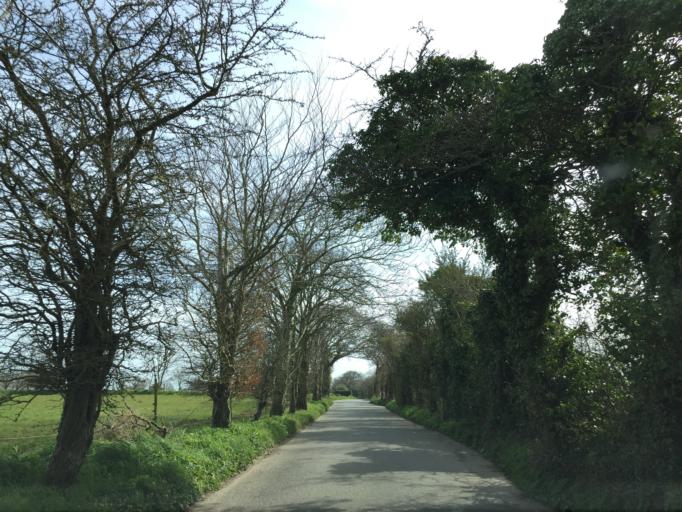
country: JE
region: St Helier
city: Saint Helier
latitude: 49.2281
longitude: -2.0565
